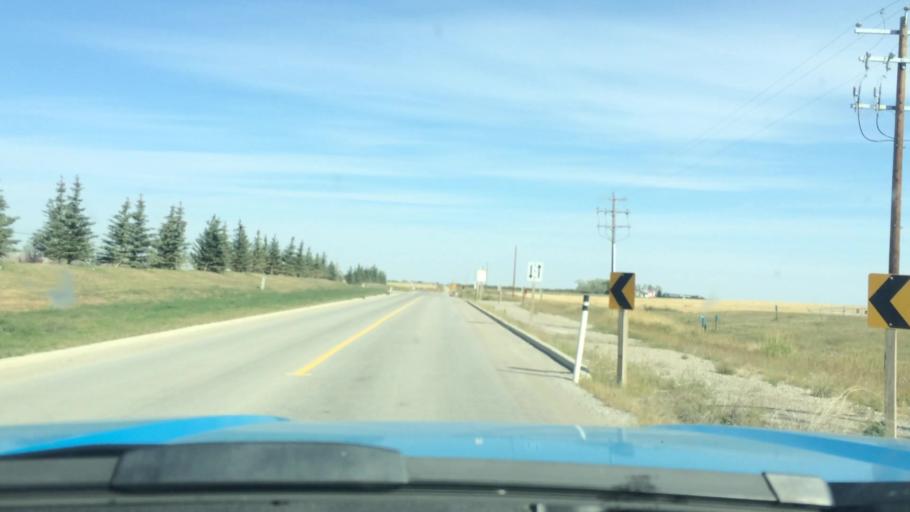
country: CA
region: Alberta
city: Airdrie
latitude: 51.2137
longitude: -113.9352
